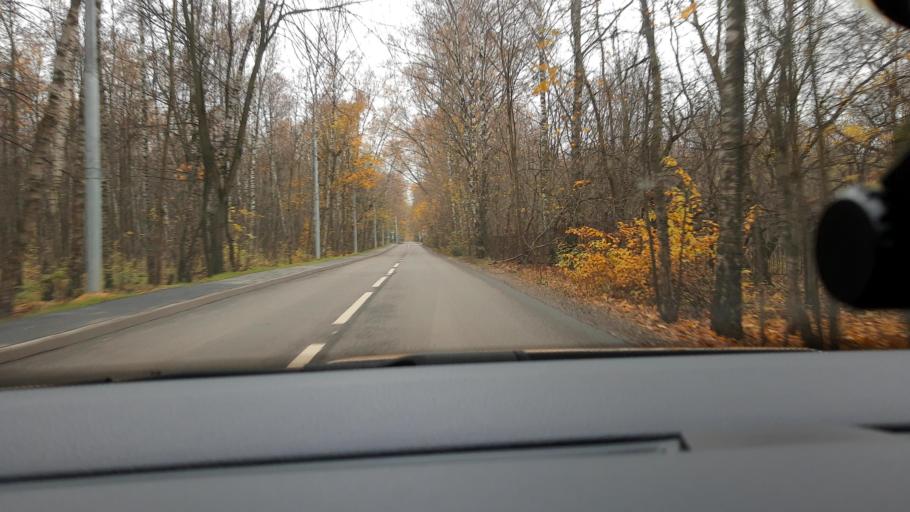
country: RU
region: Moscow
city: Rostokino
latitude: 55.8306
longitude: 37.6874
